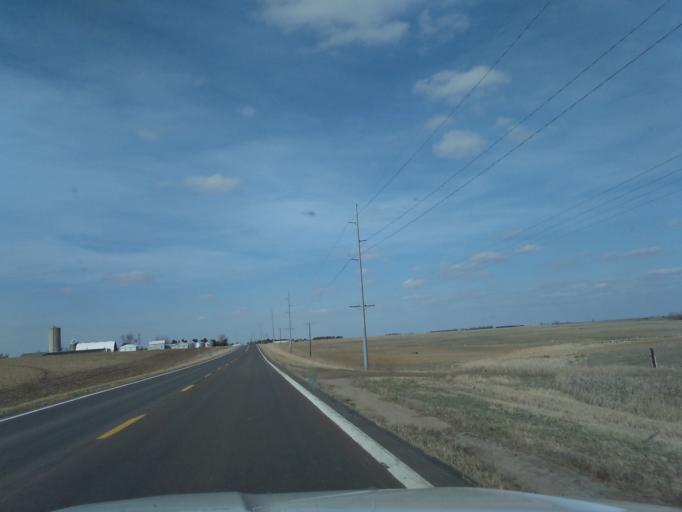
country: US
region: Nebraska
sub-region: Gage County
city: Beatrice
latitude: 40.1789
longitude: -96.9352
